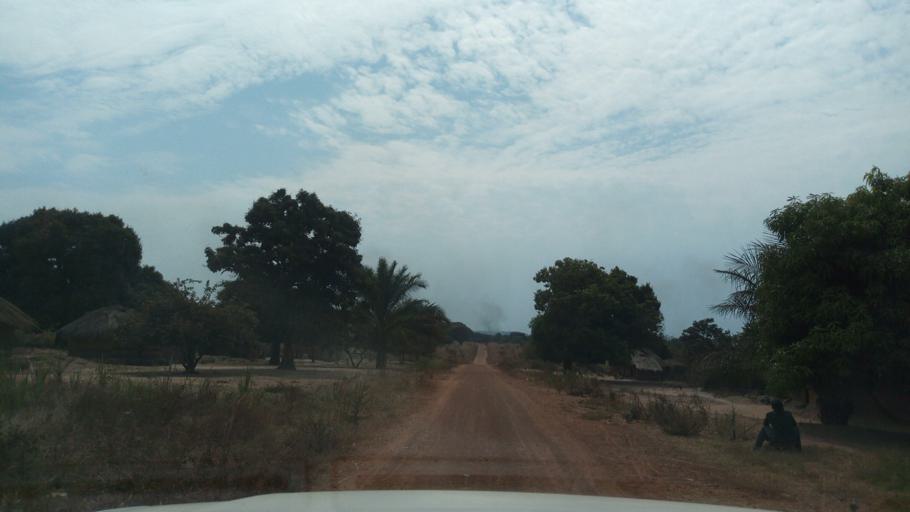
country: ZM
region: Northern
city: Kaputa
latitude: -8.3943
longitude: 28.9439
